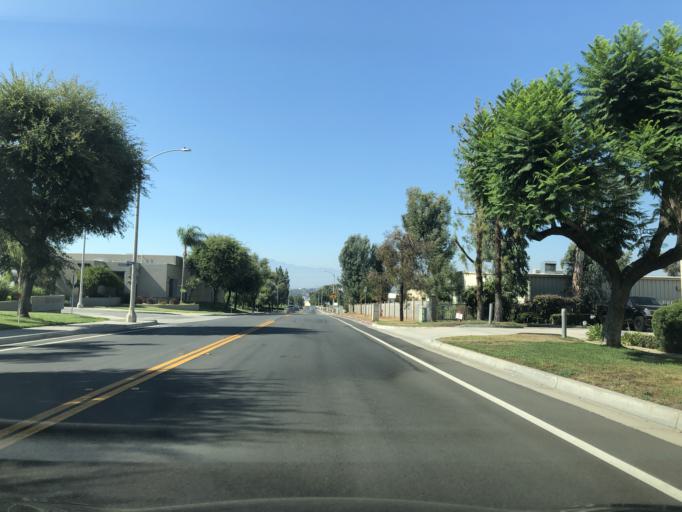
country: US
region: California
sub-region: Riverside County
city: El Cerrito
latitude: 33.8512
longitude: -117.5391
